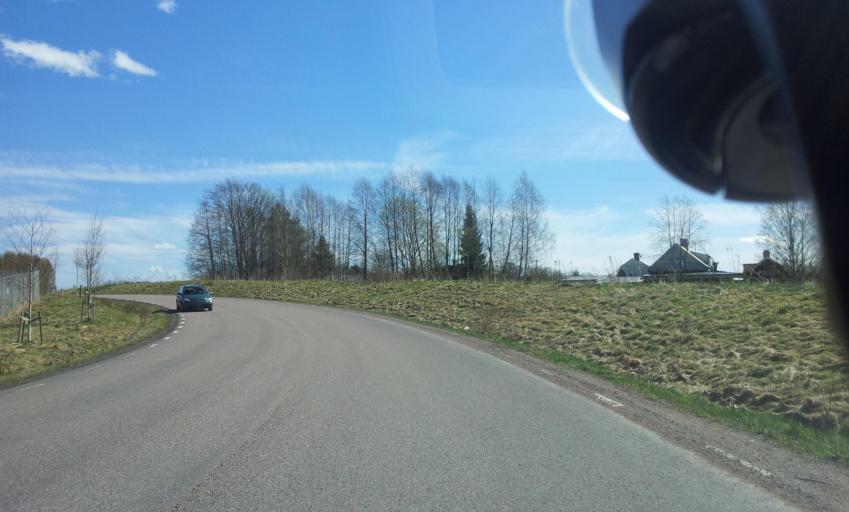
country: SE
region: Dalarna
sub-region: Borlange Kommun
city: Borlaenge
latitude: 60.4831
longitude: 15.4667
